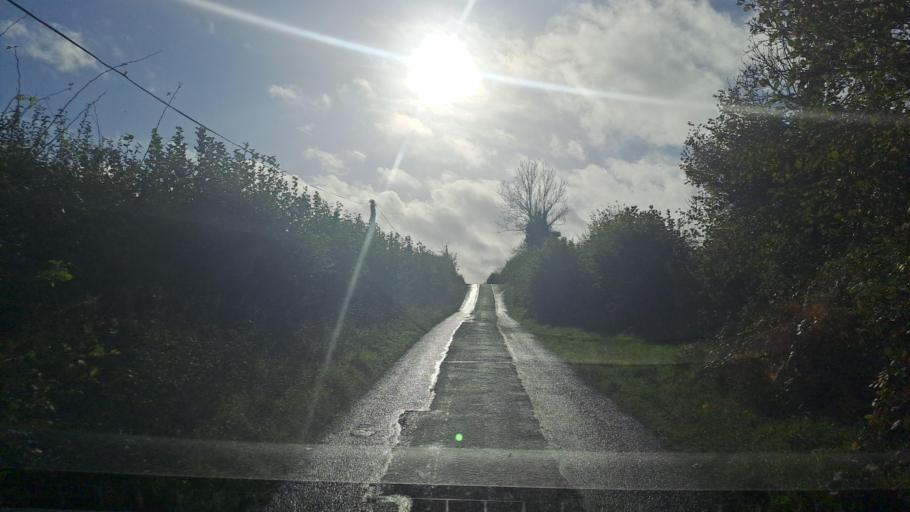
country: IE
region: Ulster
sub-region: An Cabhan
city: Cootehill
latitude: 54.0093
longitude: -7.0392
